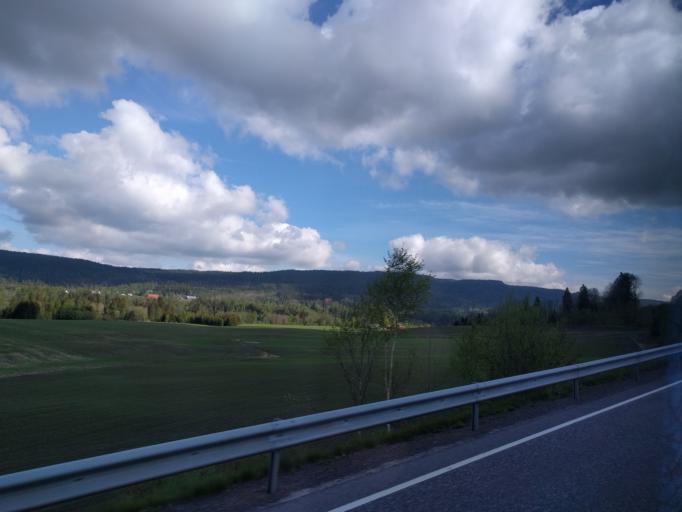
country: NO
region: Vestfold
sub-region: Lardal
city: Svarstad
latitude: 59.3930
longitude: 9.9513
